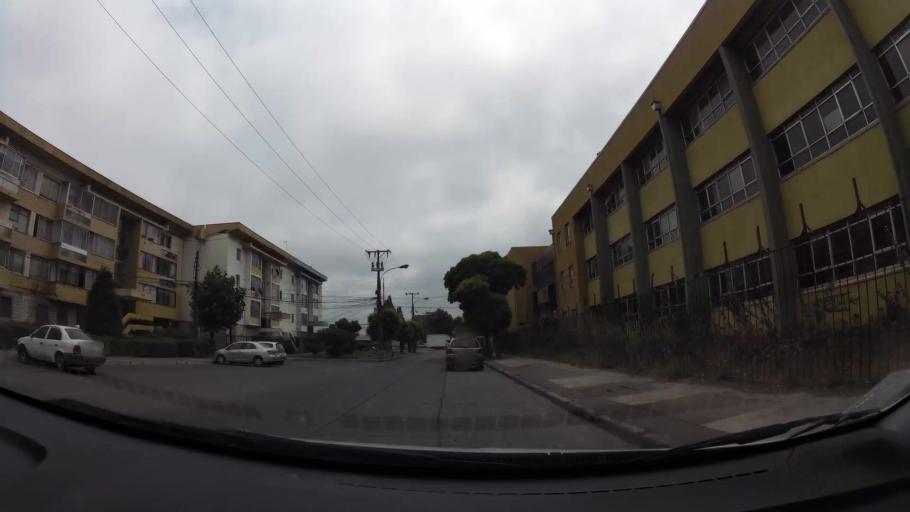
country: CL
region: Biobio
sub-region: Provincia de Concepcion
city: Concepcion
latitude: -36.8173
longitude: -73.0444
